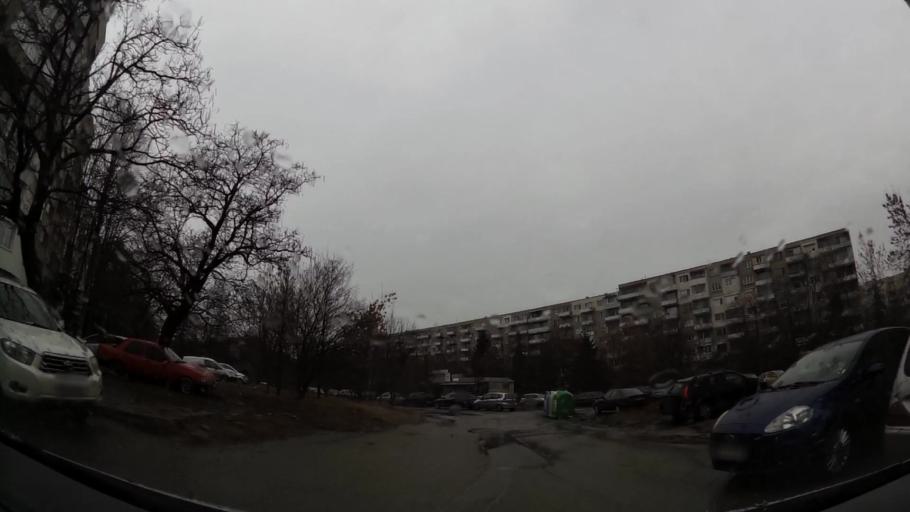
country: BG
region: Sofia-Capital
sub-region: Stolichna Obshtina
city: Sofia
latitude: 42.6561
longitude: 23.3802
